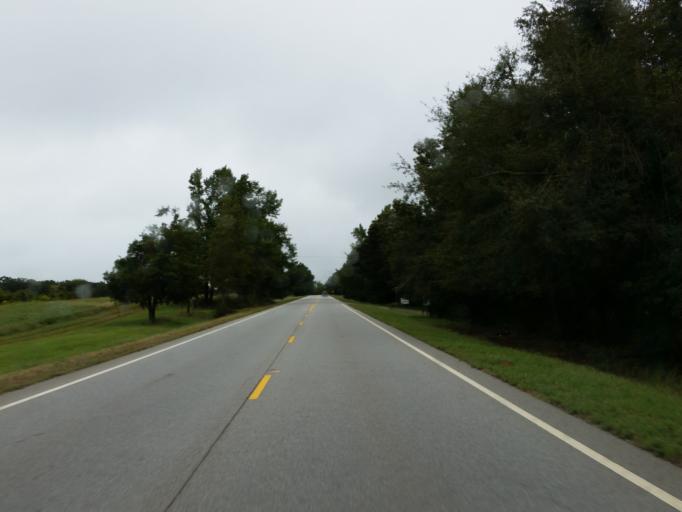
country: US
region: Georgia
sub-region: Lamar County
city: Barnesville
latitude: 32.9633
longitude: -84.1110
